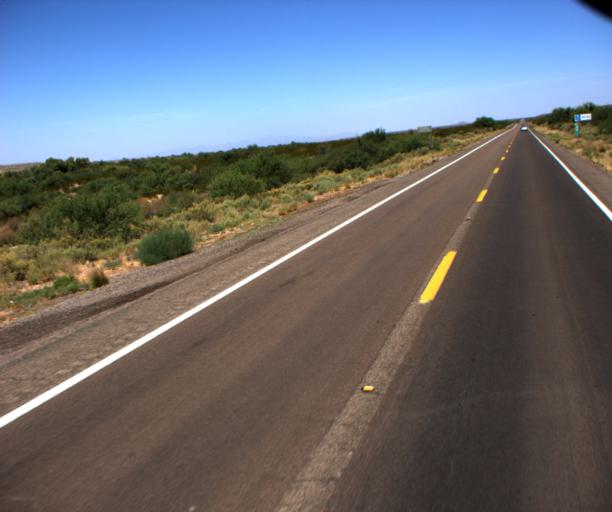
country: US
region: Arizona
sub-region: Graham County
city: Bylas
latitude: 33.1818
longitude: -110.1541
